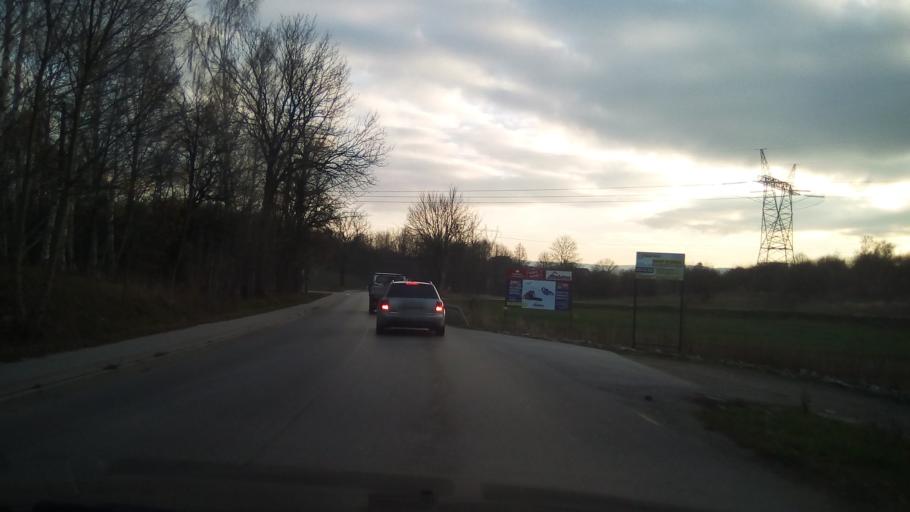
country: PL
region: Subcarpathian Voivodeship
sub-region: Powiat rzeszowski
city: Niechobrz
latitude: 50.0260
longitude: 21.8854
